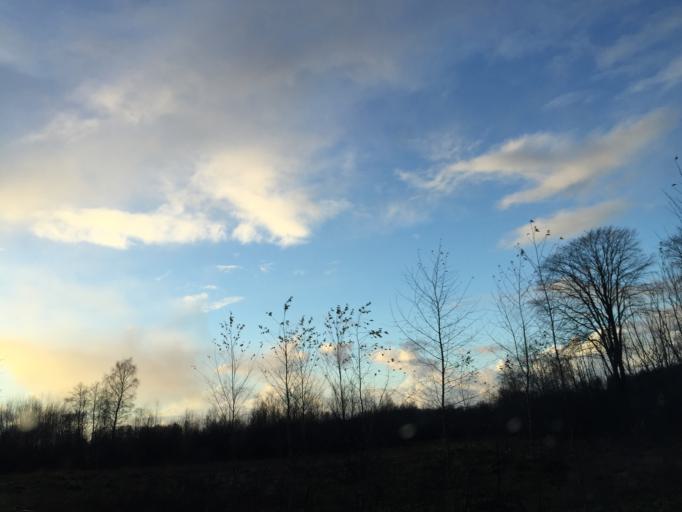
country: LV
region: Burtnieki
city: Matisi
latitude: 57.6764
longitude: 25.2104
